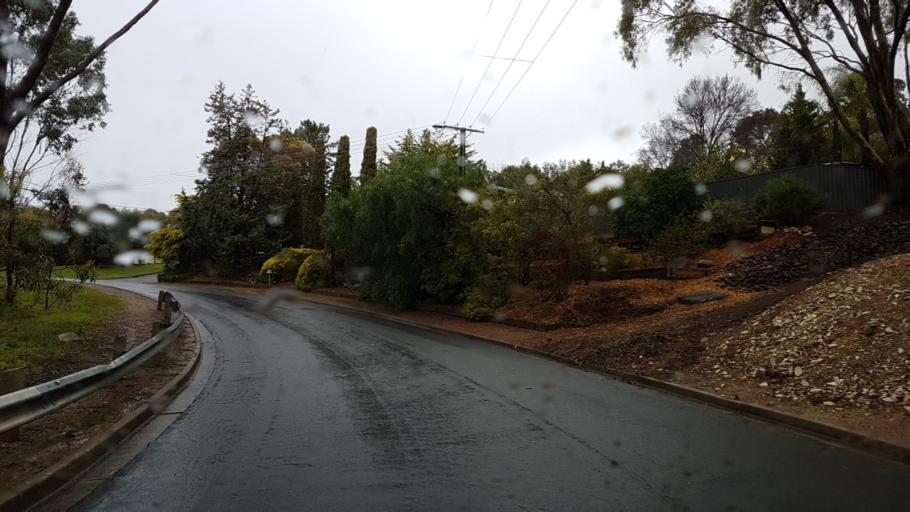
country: AU
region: South Australia
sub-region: Onkaparinga
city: Bedford Park
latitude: -35.0421
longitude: 138.5866
